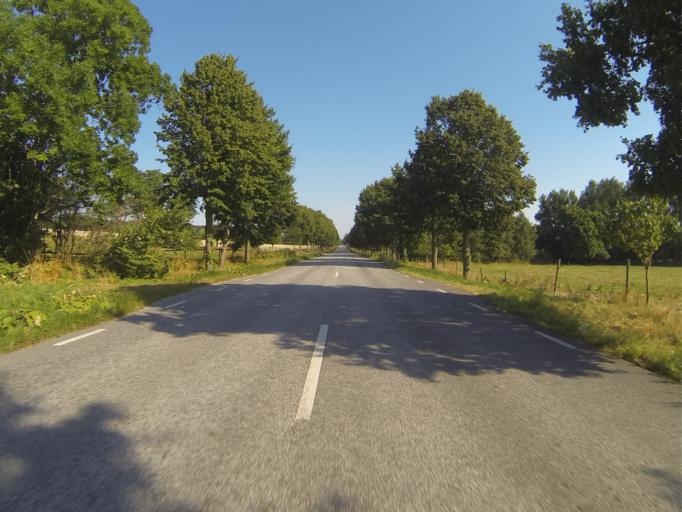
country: SE
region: Skane
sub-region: Hoors Kommun
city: Loberod
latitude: 55.7049
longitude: 13.5643
